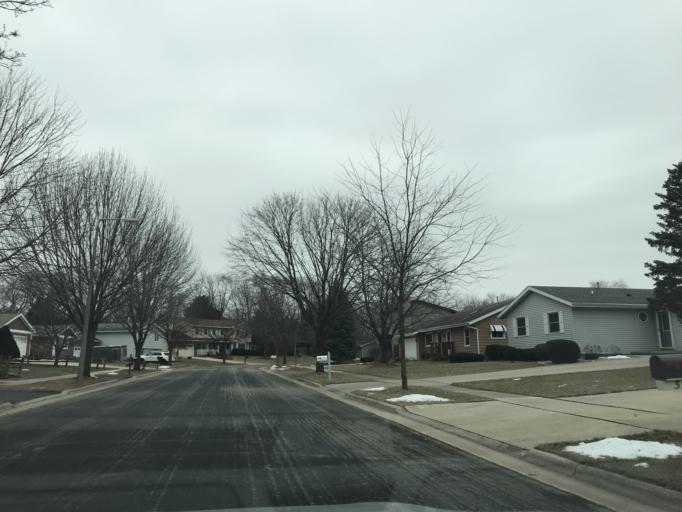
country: US
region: Wisconsin
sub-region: Dane County
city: Monona
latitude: 43.0981
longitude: -89.2934
